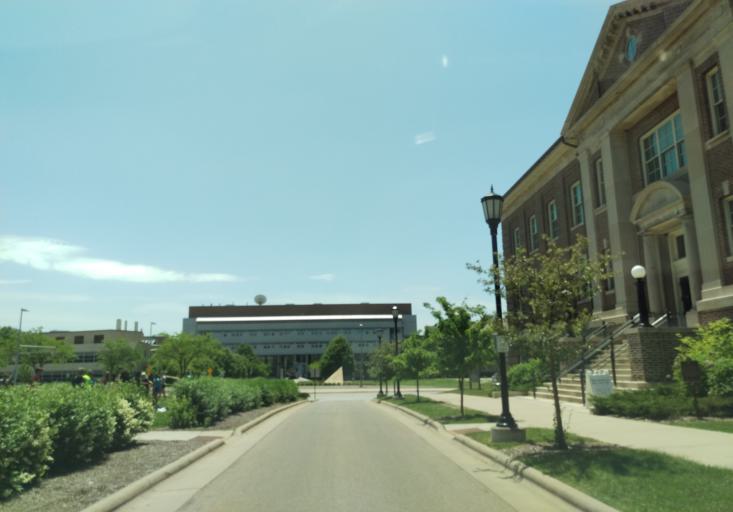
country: US
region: Wisconsin
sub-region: Dane County
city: Madison
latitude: 43.0741
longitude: -89.4104
